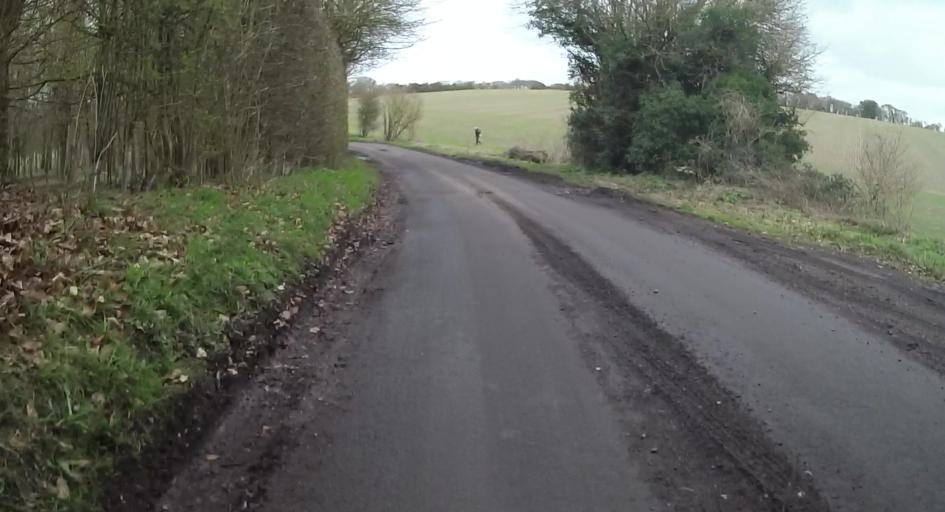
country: GB
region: England
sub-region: Hampshire
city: Kingsclere
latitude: 51.2854
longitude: -1.2254
